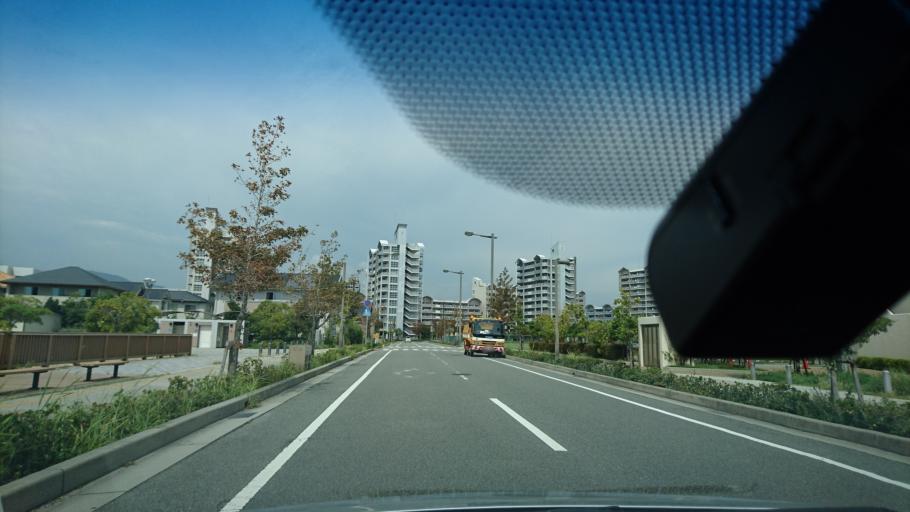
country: JP
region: Hyogo
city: Nishinomiya-hama
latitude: 34.7108
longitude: 135.3150
